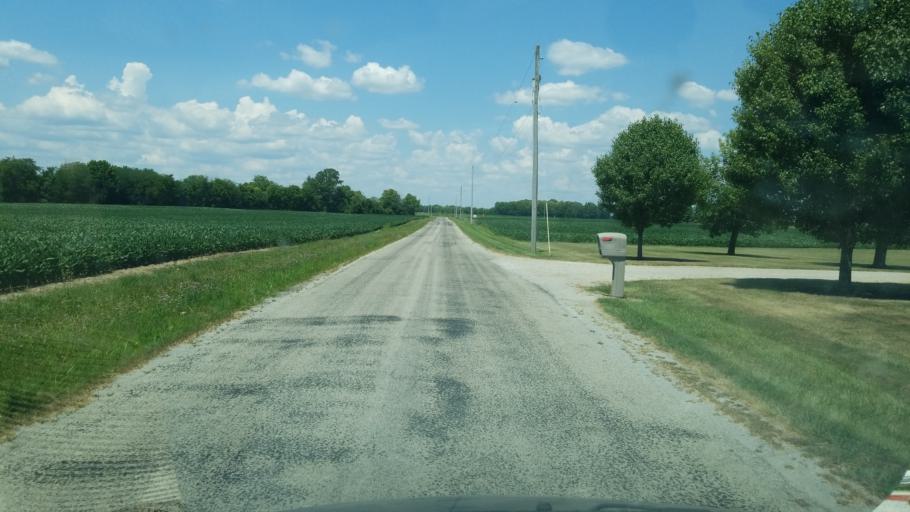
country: US
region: Ohio
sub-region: Madison County
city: Plain City
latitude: 40.0696
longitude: -83.3996
